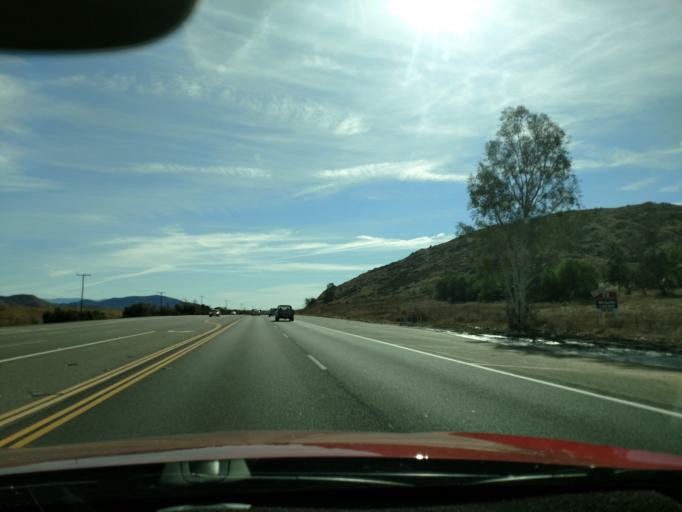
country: US
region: California
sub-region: Riverside County
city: Winchester
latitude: 33.6850
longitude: -117.0844
